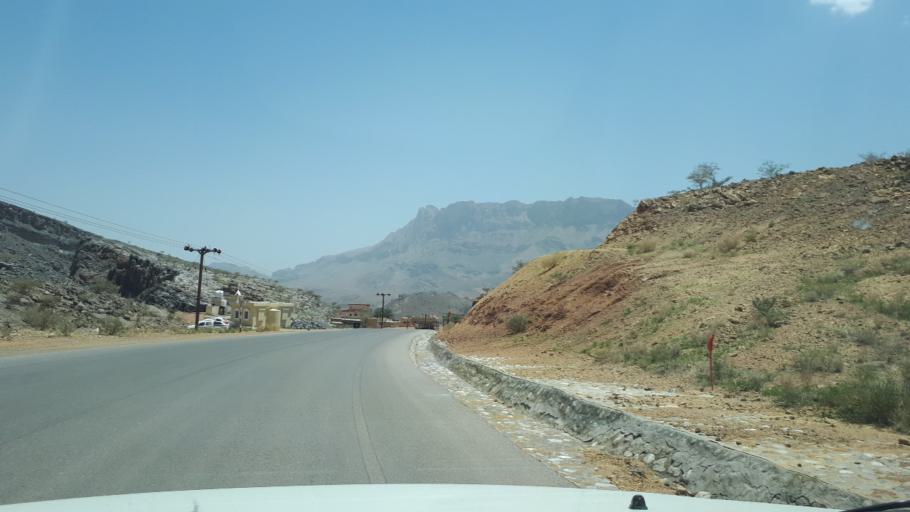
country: OM
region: Muhafazat ad Dakhiliyah
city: Bahla'
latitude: 23.1855
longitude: 57.1405
